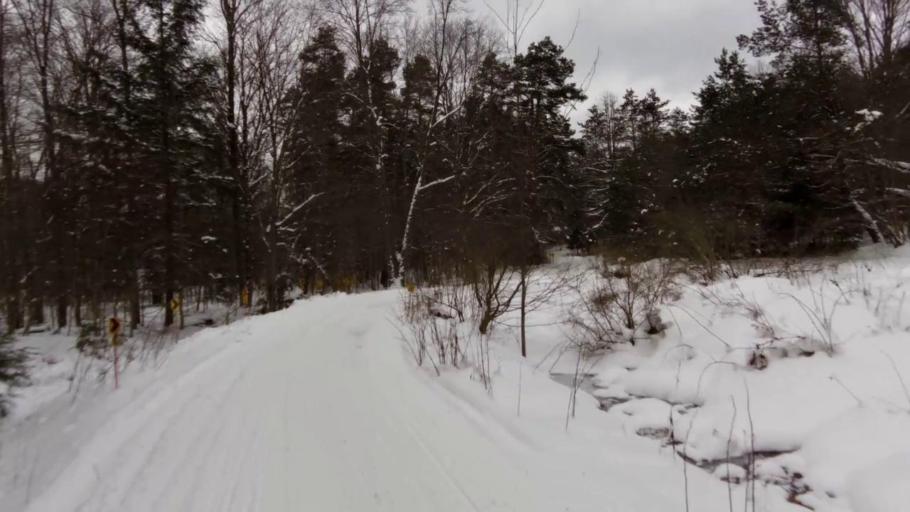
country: US
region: Pennsylvania
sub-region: McKean County
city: Bradford
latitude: 42.0212
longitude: -78.7223
